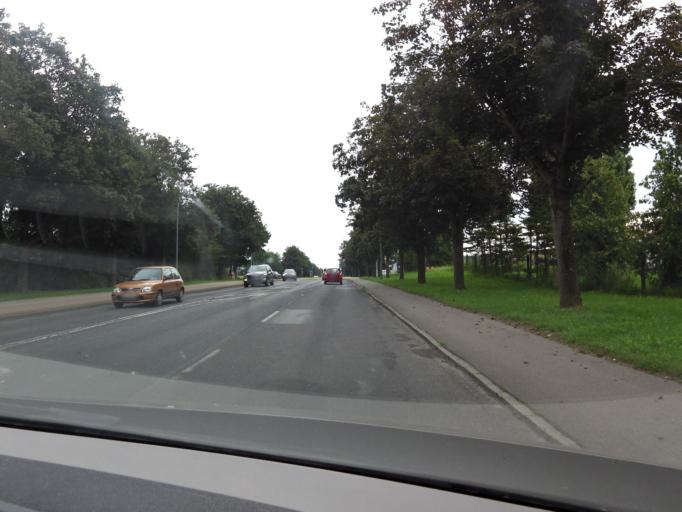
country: DE
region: Mecklenburg-Vorpommern
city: Neustrelitz
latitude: 53.3522
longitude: 13.0771
